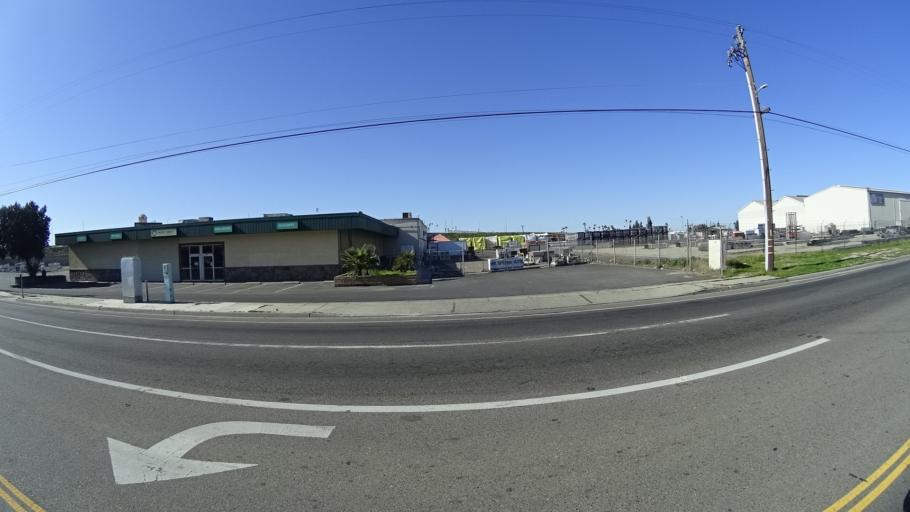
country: US
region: California
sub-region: Fresno County
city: West Park
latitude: 36.7738
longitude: -119.8359
